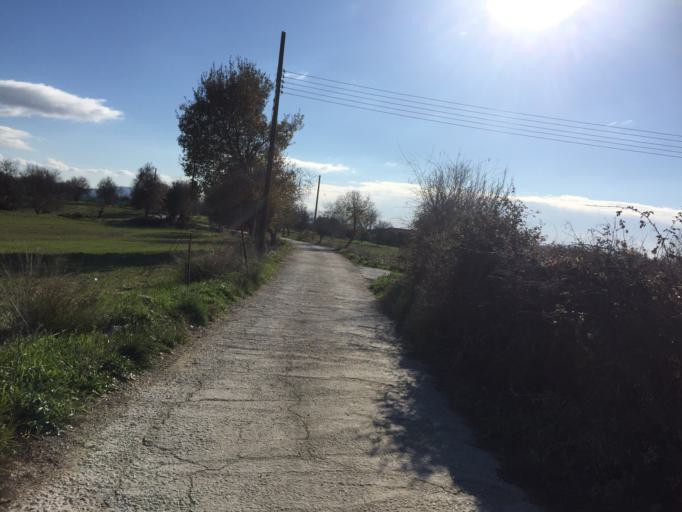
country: CY
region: Pafos
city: Mesogi
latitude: 34.8427
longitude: 32.5051
